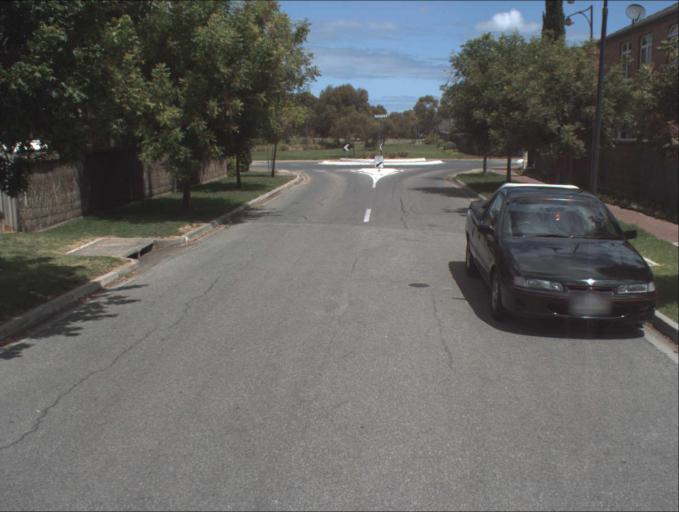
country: AU
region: South Australia
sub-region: Port Adelaide Enfield
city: Gilles Plains
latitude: -34.8546
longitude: 138.6298
